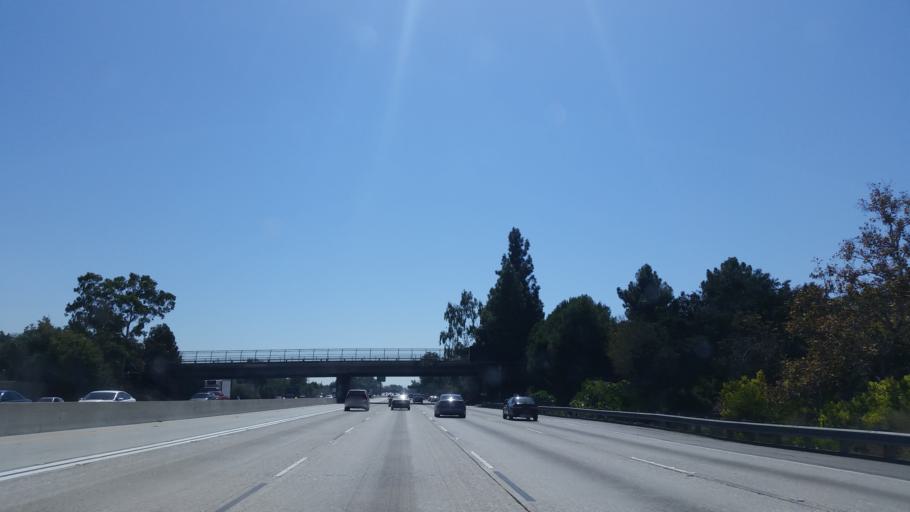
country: US
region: California
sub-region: Los Angeles County
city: Hawaiian Gardens
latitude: 33.8193
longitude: -118.0815
